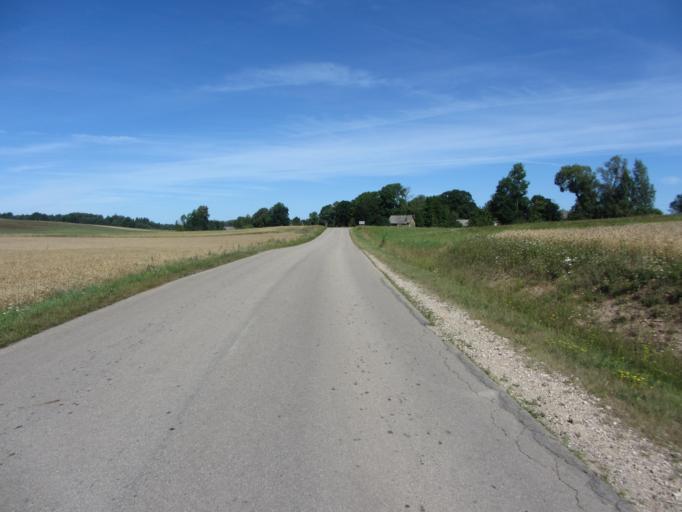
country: LT
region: Panevezys
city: Rokiskis
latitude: 55.8627
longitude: 25.7258
